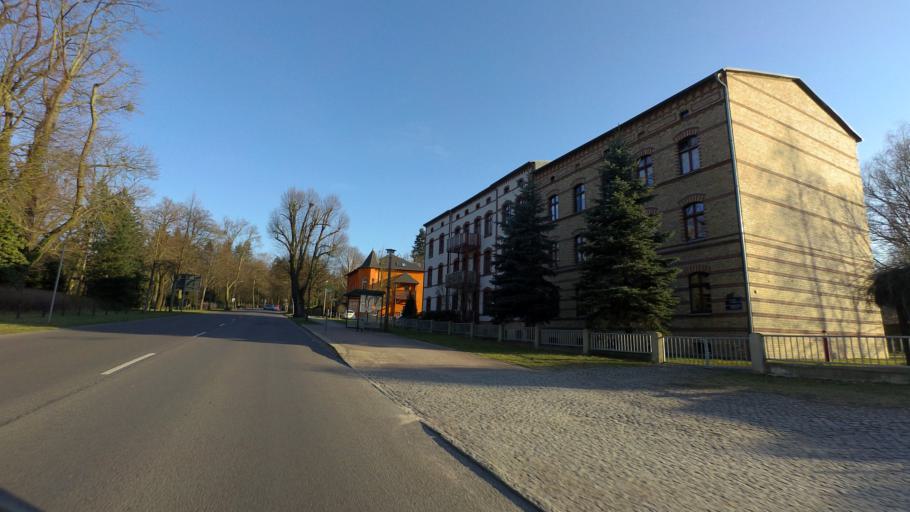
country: DE
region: Brandenburg
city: Eberswalde
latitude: 52.8288
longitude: 13.8288
